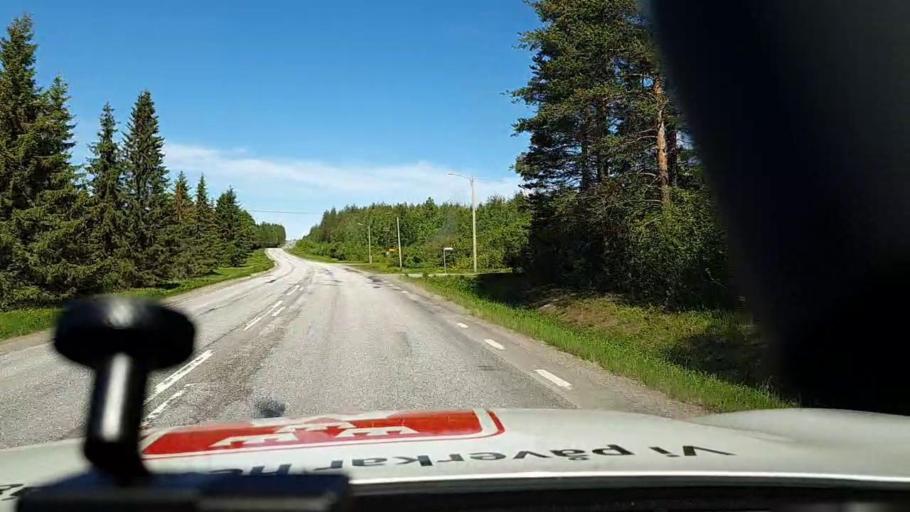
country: SE
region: Norrbotten
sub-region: Kalix Kommun
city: Toere
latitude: 66.0816
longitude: 22.7142
